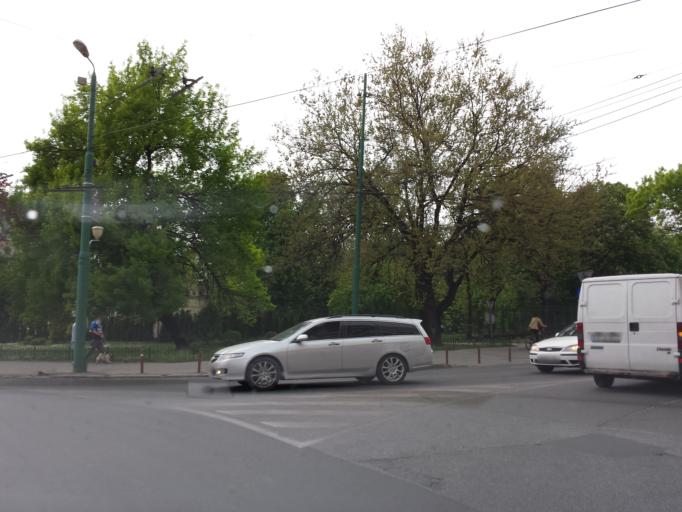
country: RO
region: Timis
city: Timisoara
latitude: 45.7598
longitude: 21.2279
